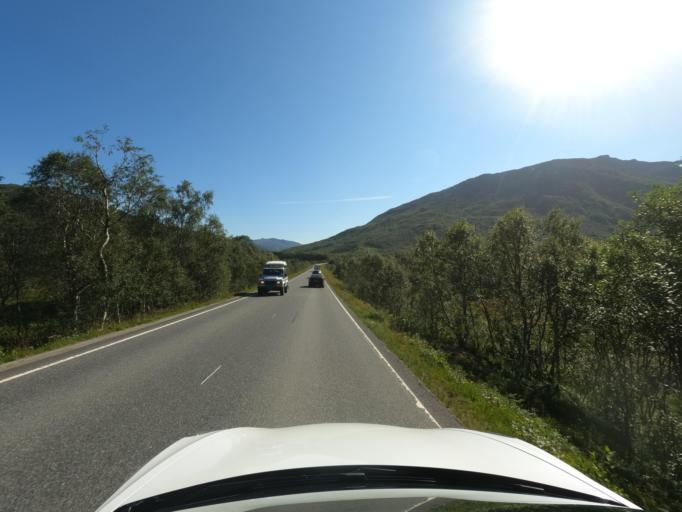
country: NO
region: Nordland
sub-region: Lodingen
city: Lodingen
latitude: 68.5300
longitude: 15.7375
